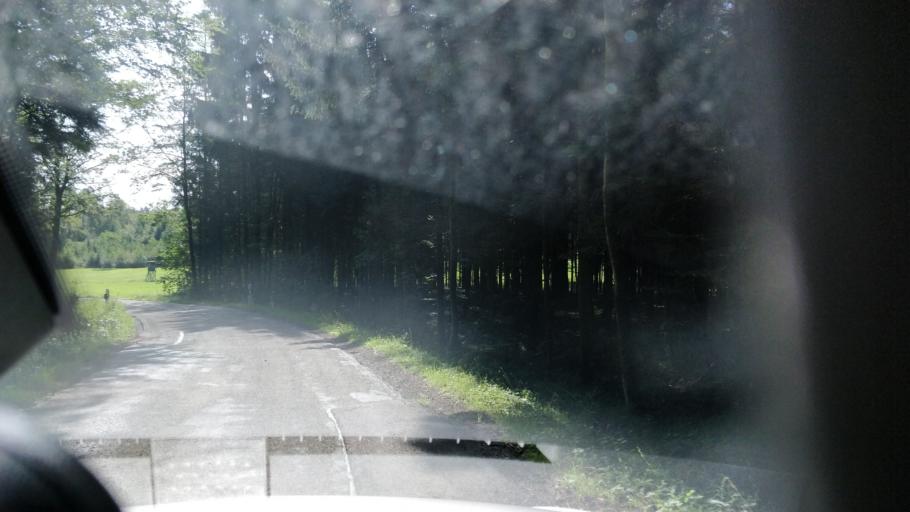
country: DE
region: Baden-Wuerttemberg
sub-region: Regierungsbezirk Stuttgart
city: Oberrot
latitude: 49.0137
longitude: 9.6283
